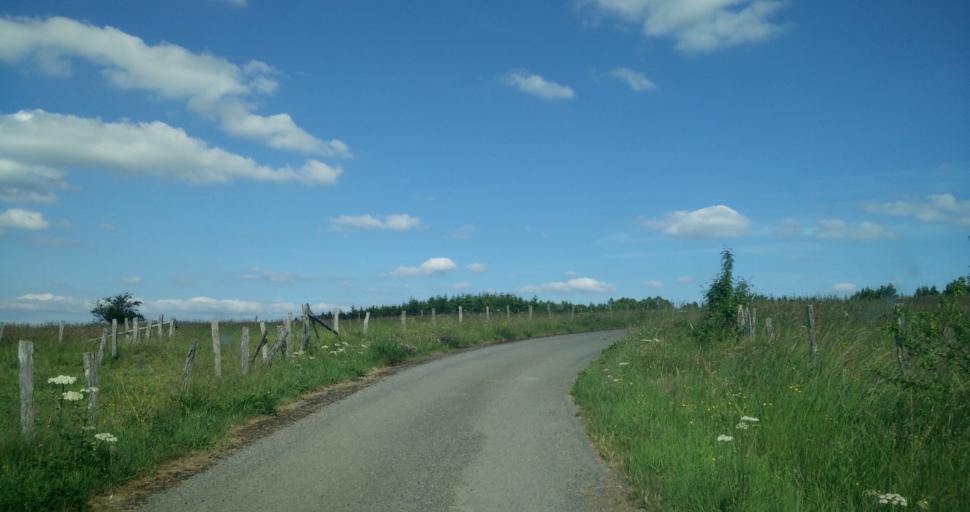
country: BE
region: Wallonia
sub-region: Province du Luxembourg
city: Houffalize
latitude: 50.1454
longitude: 5.7226
